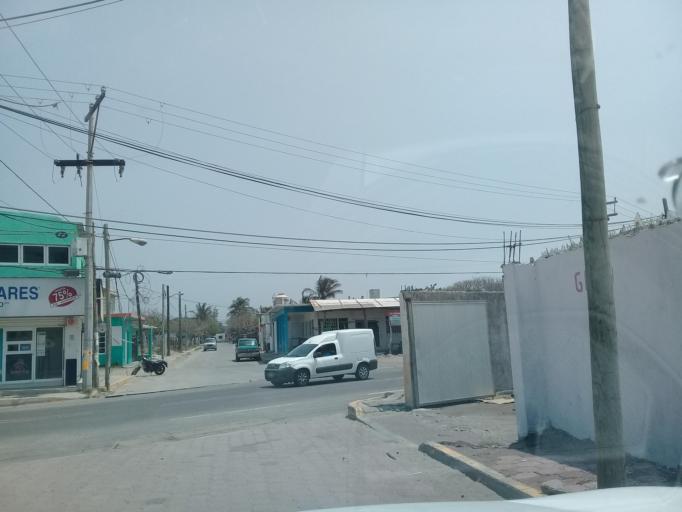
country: MX
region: Veracruz
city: Anton Lizardo
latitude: 19.0604
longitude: -95.9949
